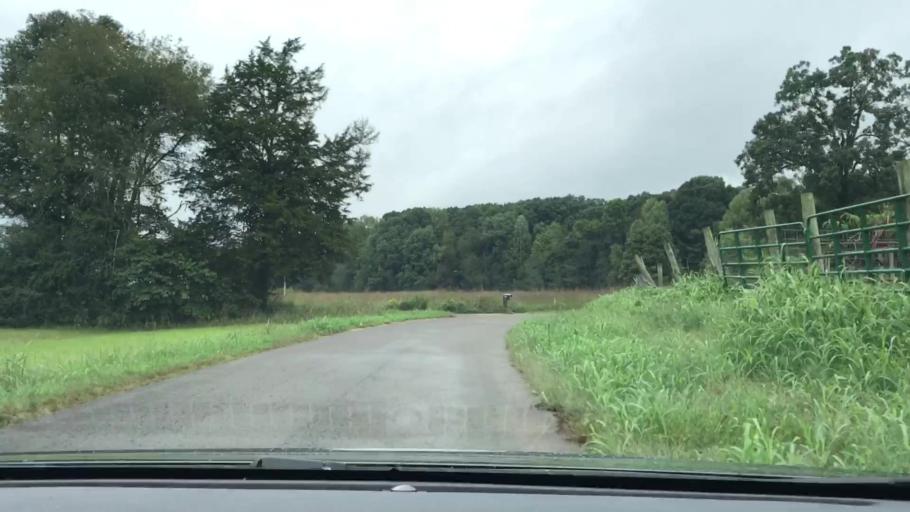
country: US
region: Kentucky
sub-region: Monroe County
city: Tompkinsville
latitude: 36.6238
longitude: -85.7723
